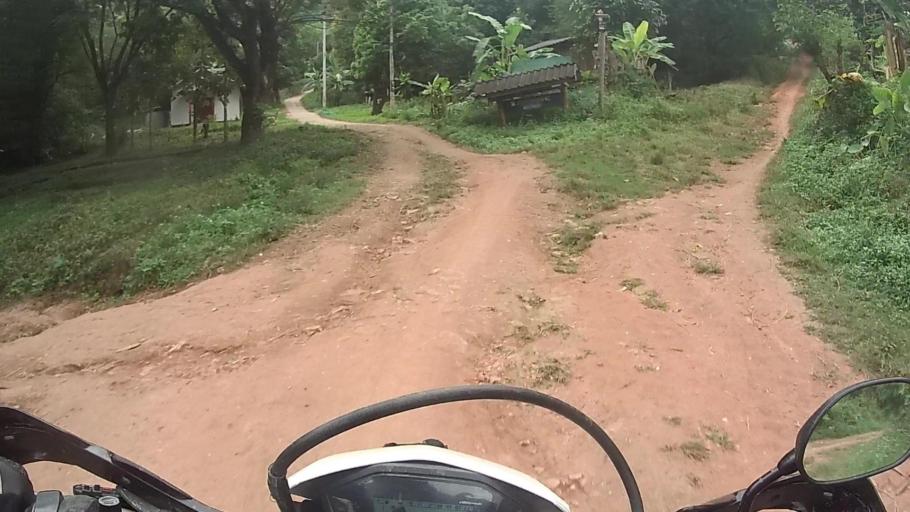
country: TH
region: Lampang
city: Mueang Pan
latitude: 18.9667
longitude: 99.4997
